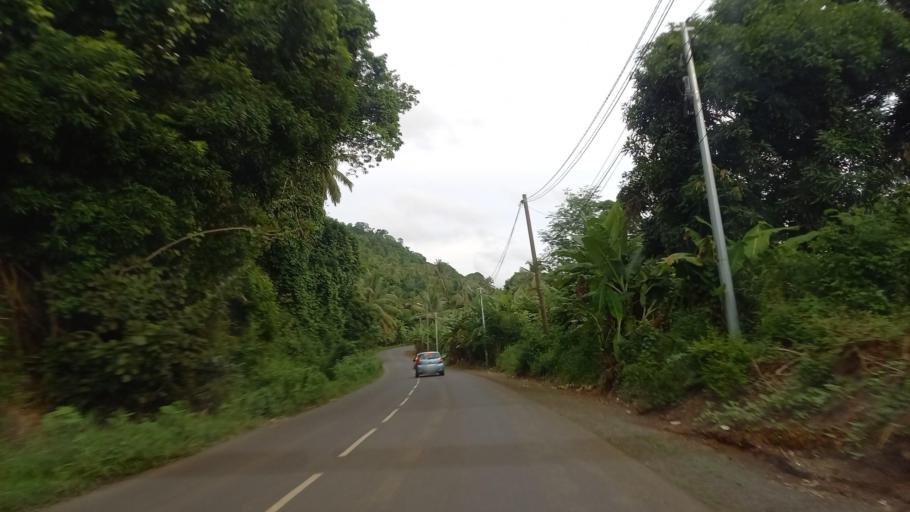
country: YT
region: Sada
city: Sada
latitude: -12.8575
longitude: 45.1018
